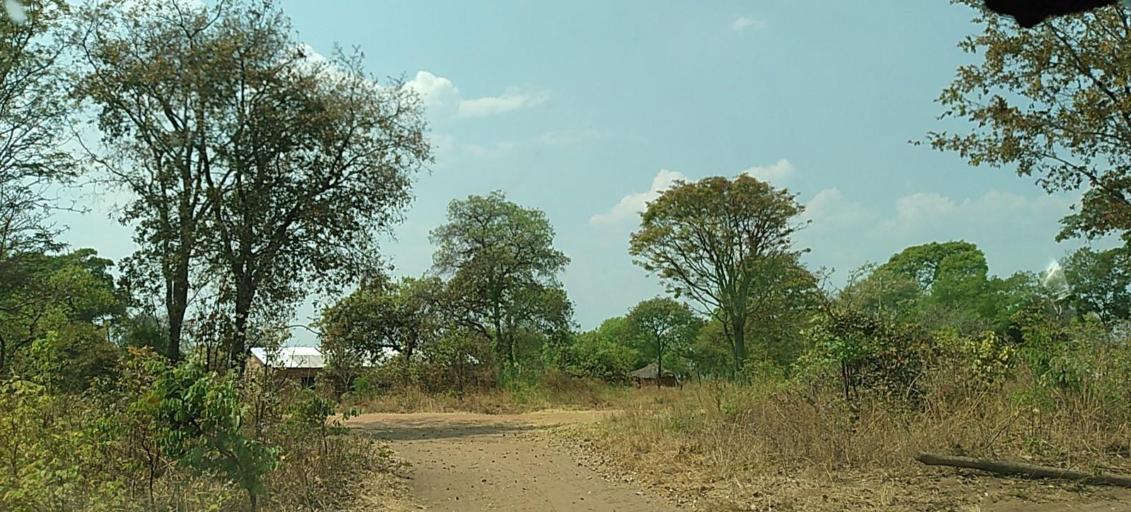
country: ZM
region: North-Western
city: Kabompo
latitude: -13.5394
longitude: 24.3551
